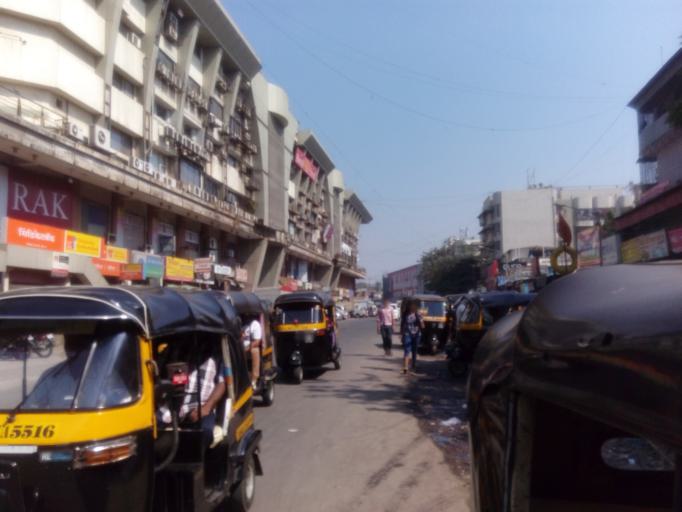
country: IN
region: Maharashtra
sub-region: Mumbai Suburban
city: Mumbai
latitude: 19.0898
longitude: 72.8370
